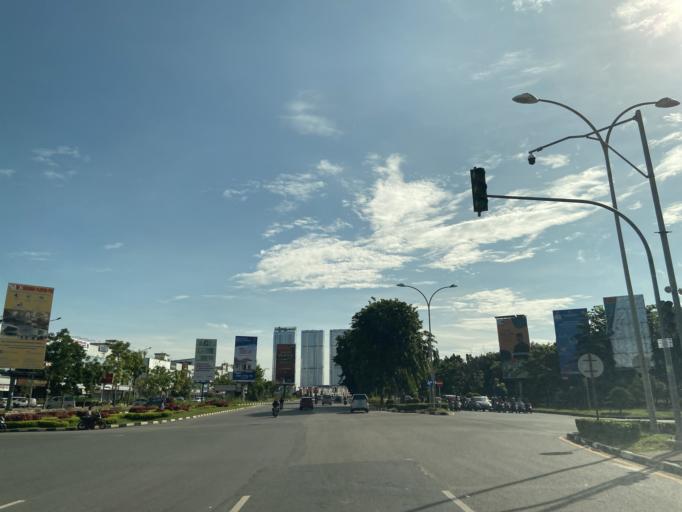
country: SG
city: Singapore
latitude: 1.1106
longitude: 104.0418
